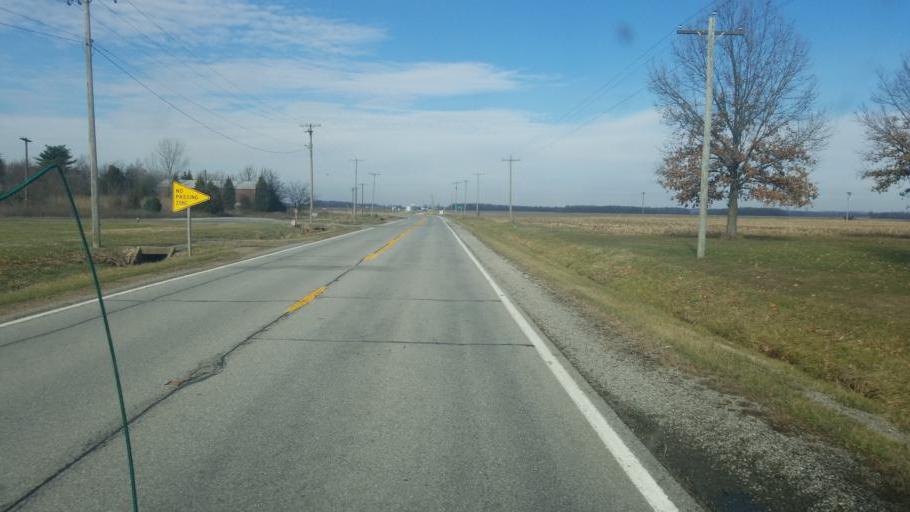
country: US
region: Illinois
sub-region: Saline County
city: Eldorado
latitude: 37.9341
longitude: -88.4576
